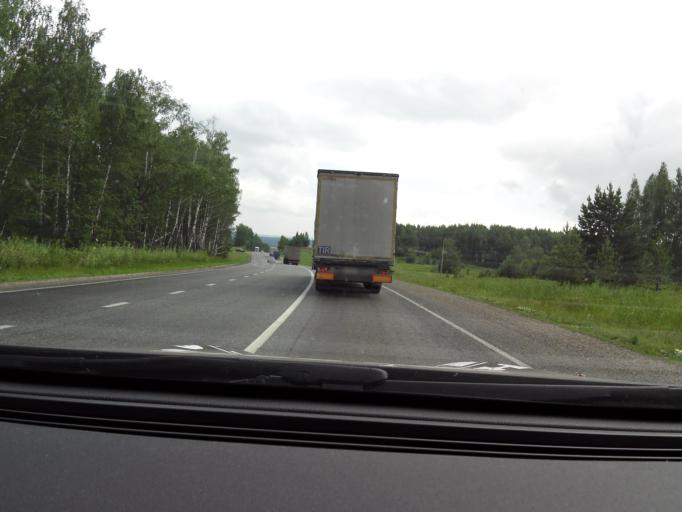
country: RU
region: Perm
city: Suksun
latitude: 57.0865
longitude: 57.3976
